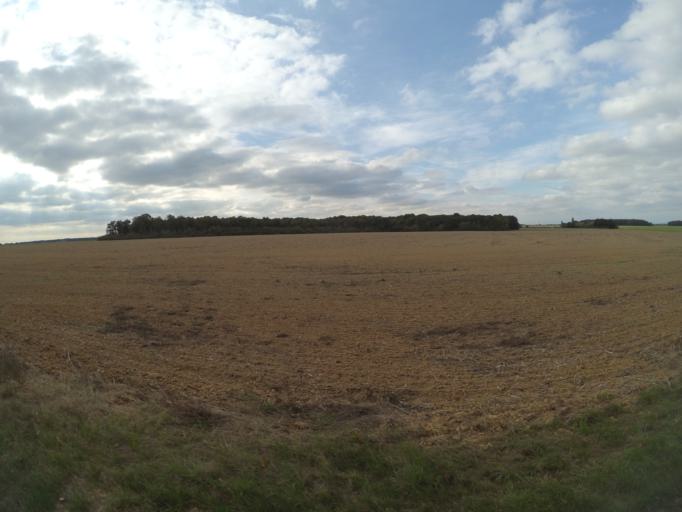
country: FR
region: Centre
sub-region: Departement d'Indre-et-Loire
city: Nazelles-Negron
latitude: 47.4667
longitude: 0.9389
